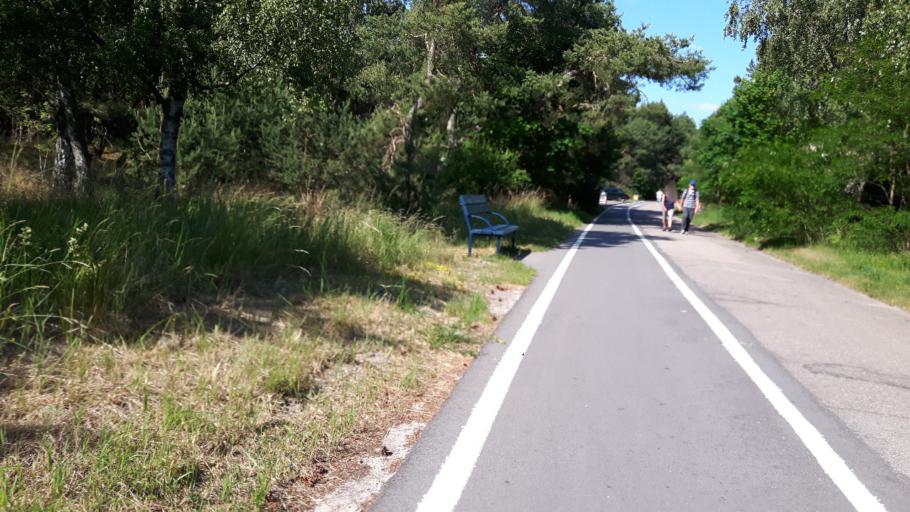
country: LT
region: Klaipedos apskritis
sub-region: Klaipeda
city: Klaipeda
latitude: 55.6984
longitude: 21.1028
